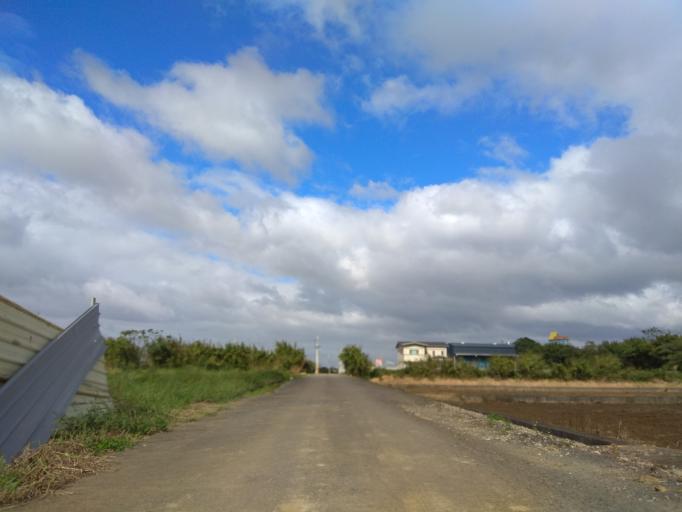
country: TW
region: Taiwan
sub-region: Hsinchu
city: Zhubei
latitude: 24.9695
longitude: 121.0928
